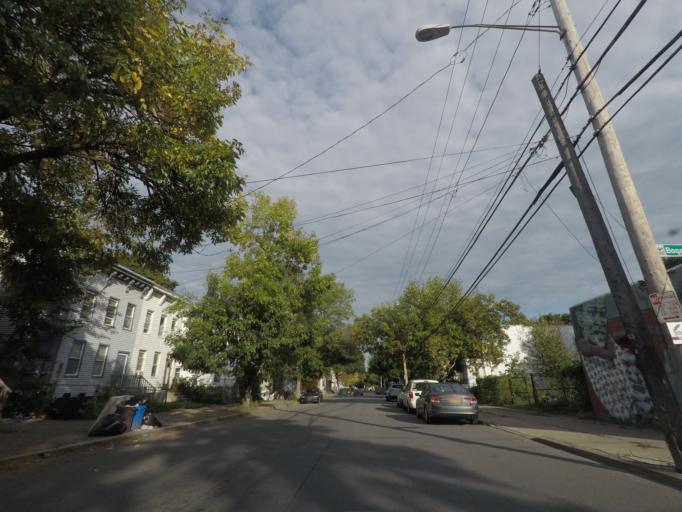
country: US
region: New York
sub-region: Albany County
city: Albany
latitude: 42.6392
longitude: -73.7714
